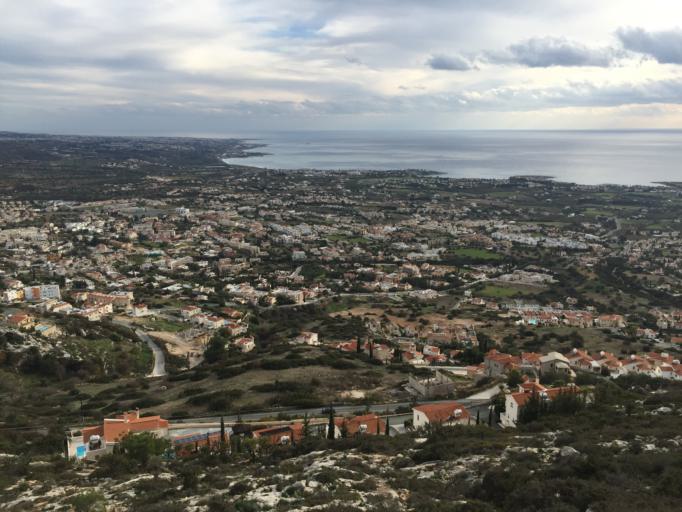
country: CY
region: Pafos
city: Pegeia
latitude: 34.8892
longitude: 32.3745
